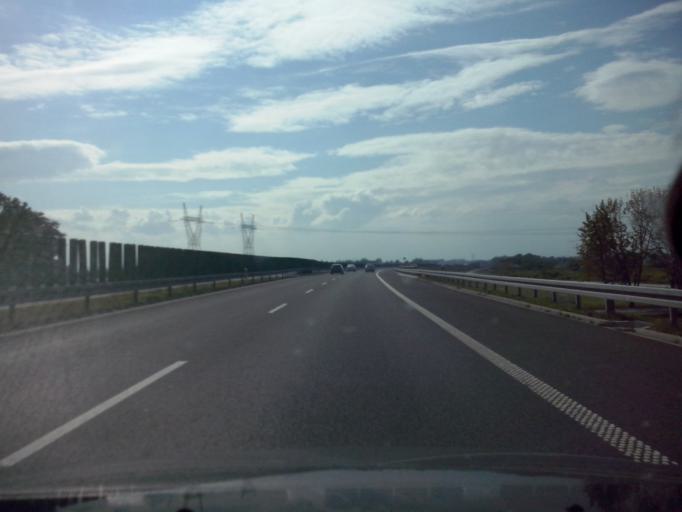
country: PL
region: Lesser Poland Voivodeship
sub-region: Powiat tarnowski
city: Lukowa
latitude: 50.0594
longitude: 20.9460
